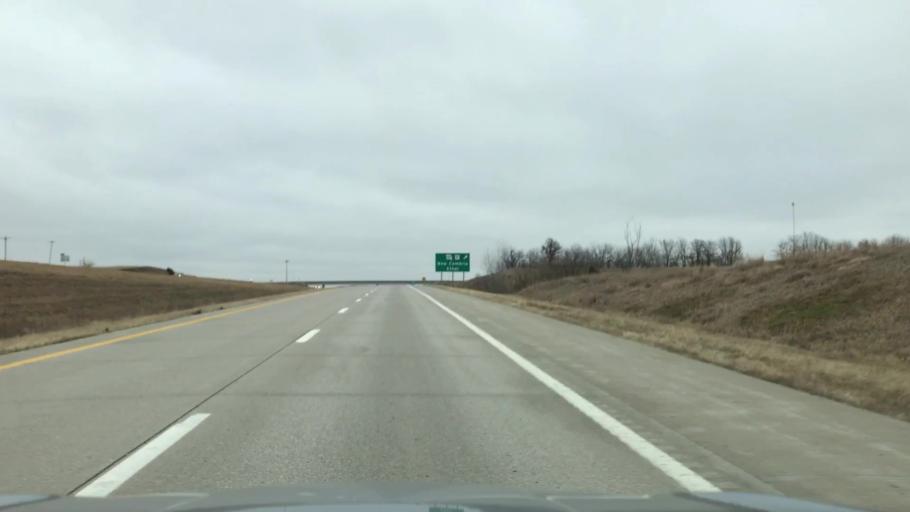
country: US
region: Missouri
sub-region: Linn County
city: Marceline
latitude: 39.7650
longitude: -92.7569
